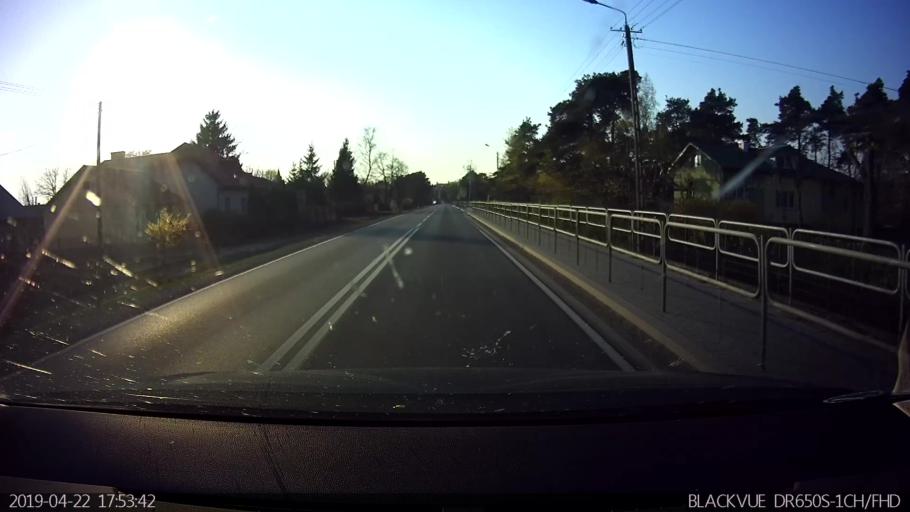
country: PL
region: Masovian Voivodeship
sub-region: Powiat wegrowski
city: Liw
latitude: 52.4548
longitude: 21.9502
